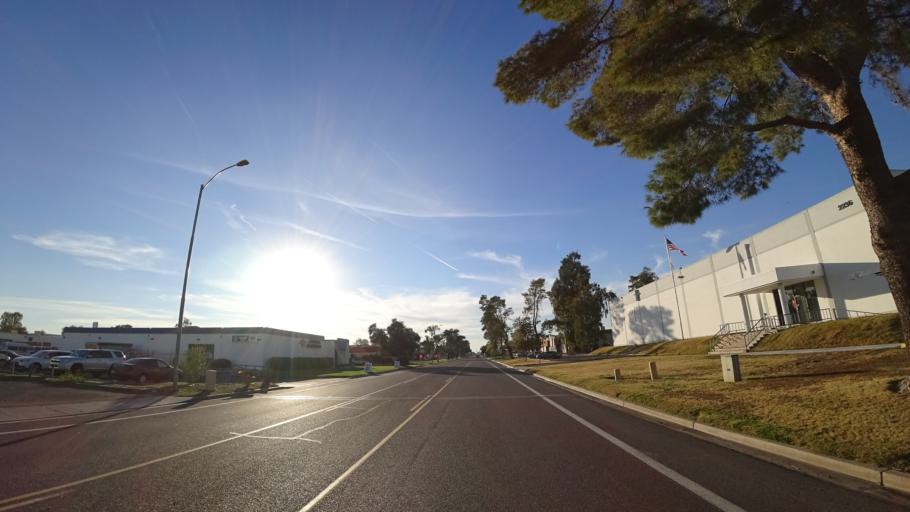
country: US
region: Arizona
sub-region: Maricopa County
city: Phoenix
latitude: 33.4240
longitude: -112.0328
